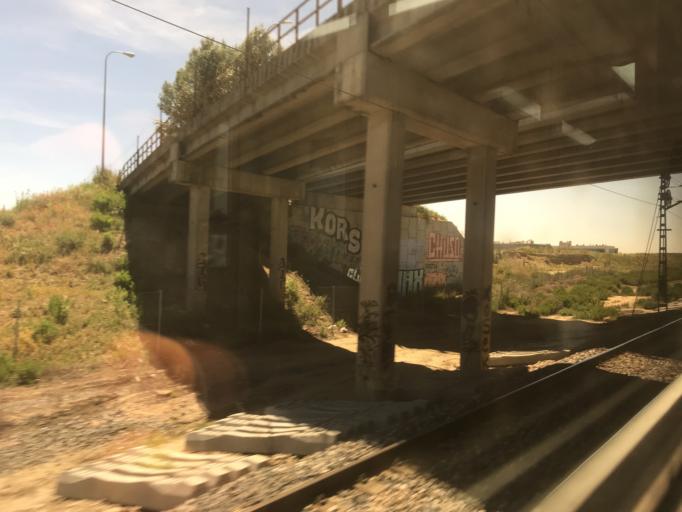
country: ES
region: Madrid
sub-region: Provincia de Madrid
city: Getafe
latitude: 40.2951
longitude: -3.7060
